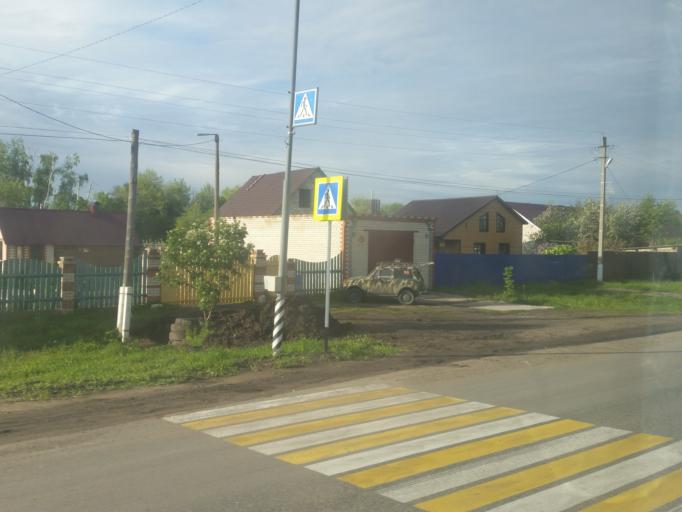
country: RU
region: Ulyanovsk
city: Mirnyy
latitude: 54.3697
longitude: 48.7227
